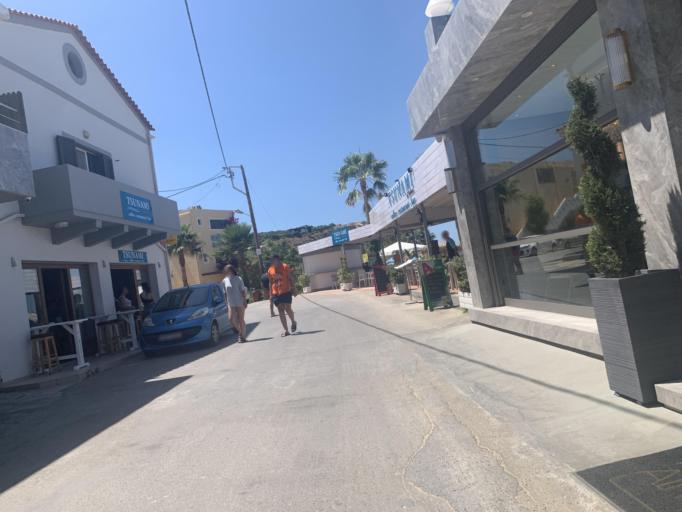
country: GR
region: Crete
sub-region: Nomos Chanias
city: Kalivai
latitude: 35.4495
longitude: 24.1989
